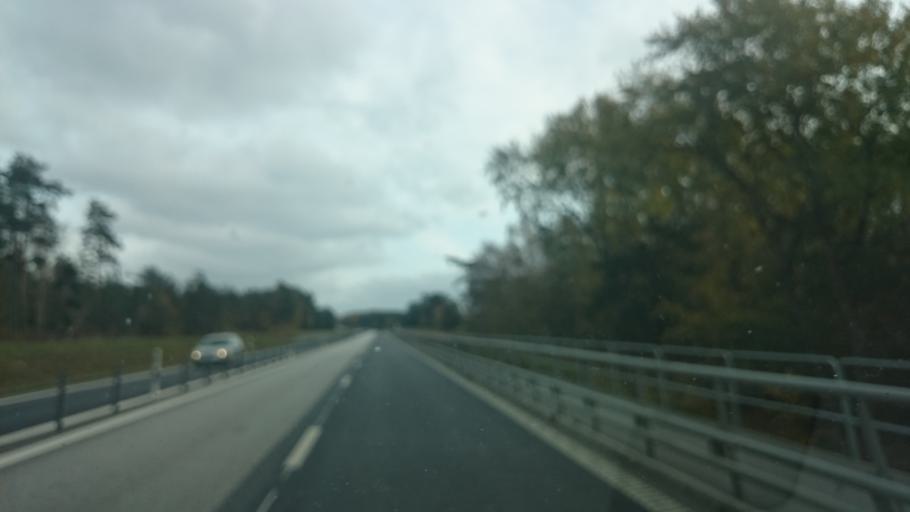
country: SE
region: Skane
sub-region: Sjobo Kommun
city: Blentarp
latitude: 55.6389
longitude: 13.5640
